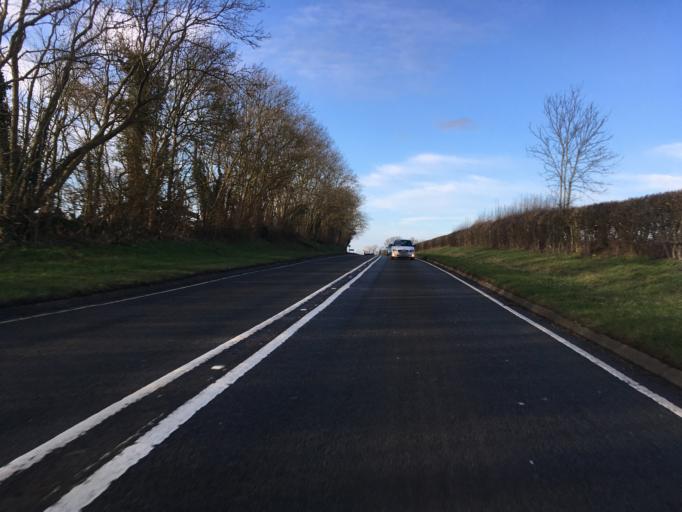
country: GB
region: England
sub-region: Warwickshire
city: Stratford-upon-Avon
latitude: 52.2200
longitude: -1.7321
